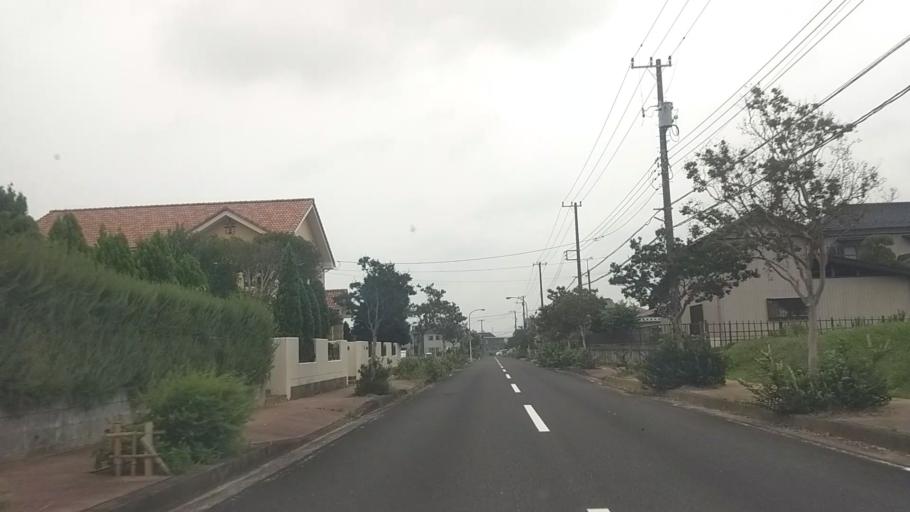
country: JP
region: Chiba
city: Kisarazu
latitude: 35.3831
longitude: 139.9651
